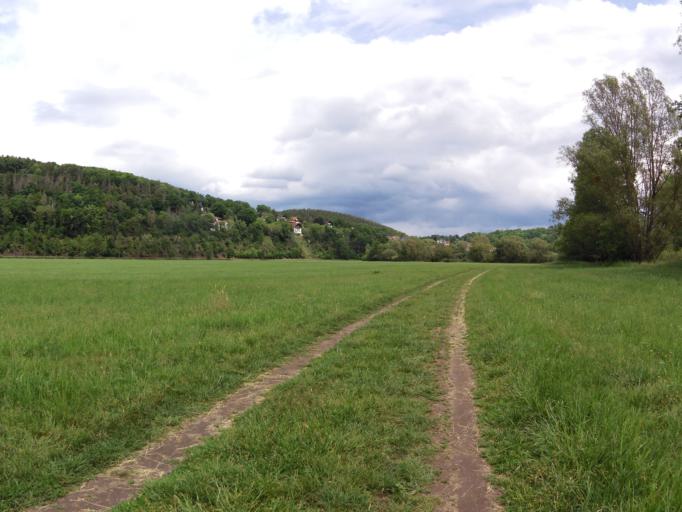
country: DE
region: Thuringia
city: Bad Salzungen
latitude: 50.8168
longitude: 10.2438
